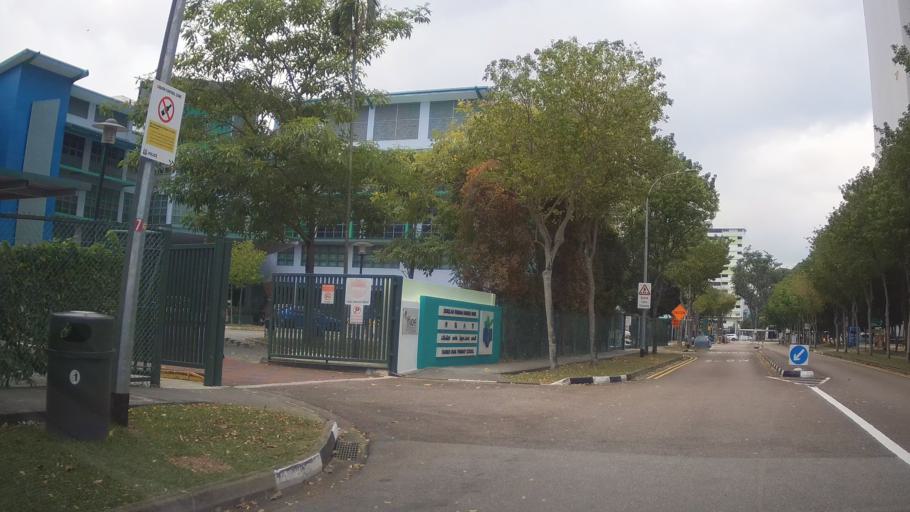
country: SG
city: Singapore
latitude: 1.3115
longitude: 103.8507
